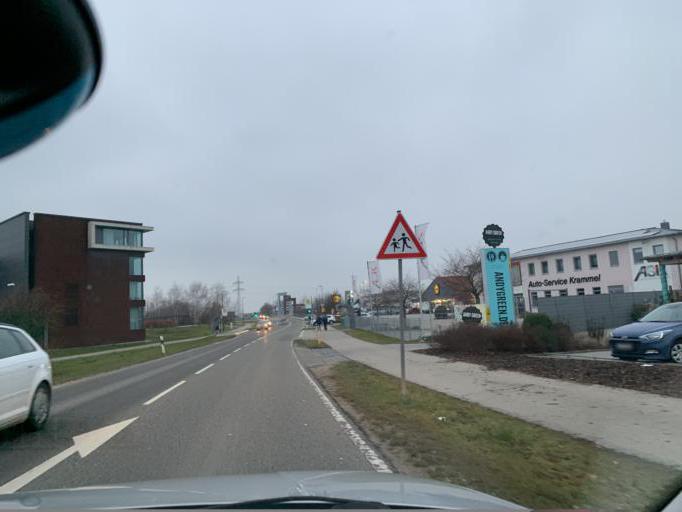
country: DE
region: Bavaria
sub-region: Upper Bavaria
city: Hepberg
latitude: 48.8091
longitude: 11.4842
